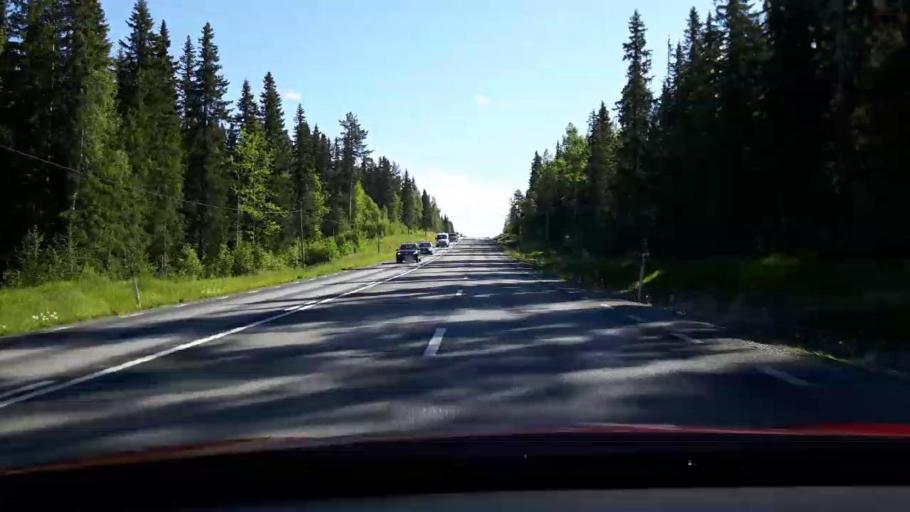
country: SE
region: Jaemtland
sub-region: OEstersunds Kommun
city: Ostersund
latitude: 63.2105
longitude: 14.7089
